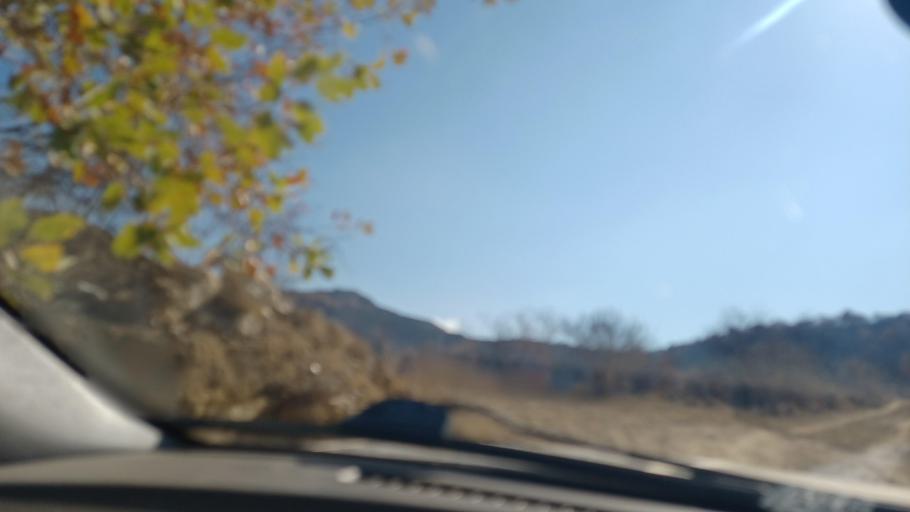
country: CY
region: Pafos
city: Polis
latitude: 34.9454
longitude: 32.4853
